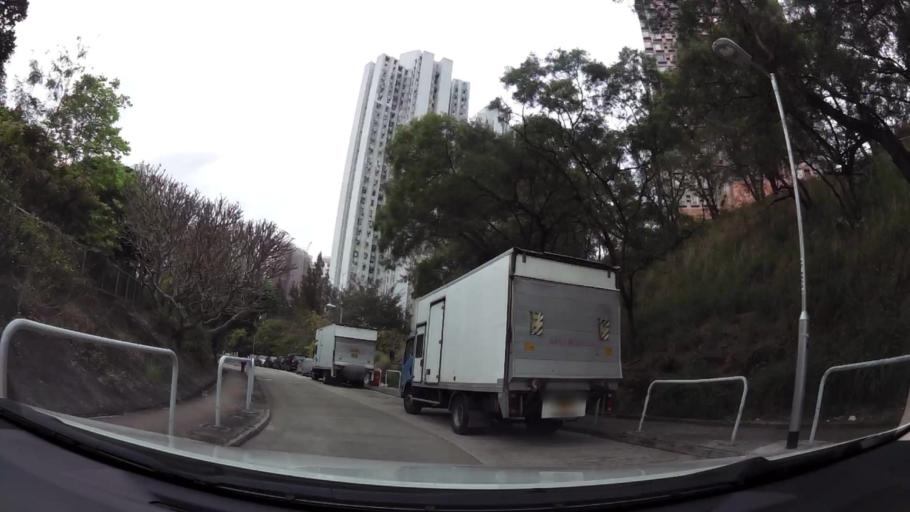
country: HK
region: Tuen Mun
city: Tuen Mun
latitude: 22.4014
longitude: 113.9801
